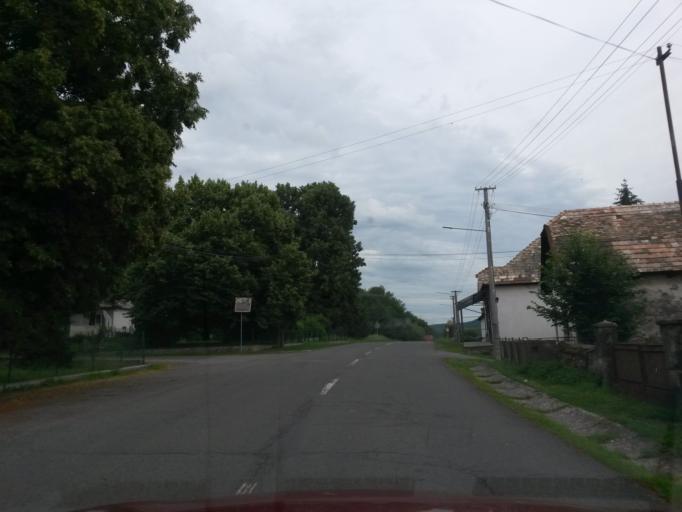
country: SK
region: Banskobystricky
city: Velky Krtis
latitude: 48.2990
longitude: 19.4018
